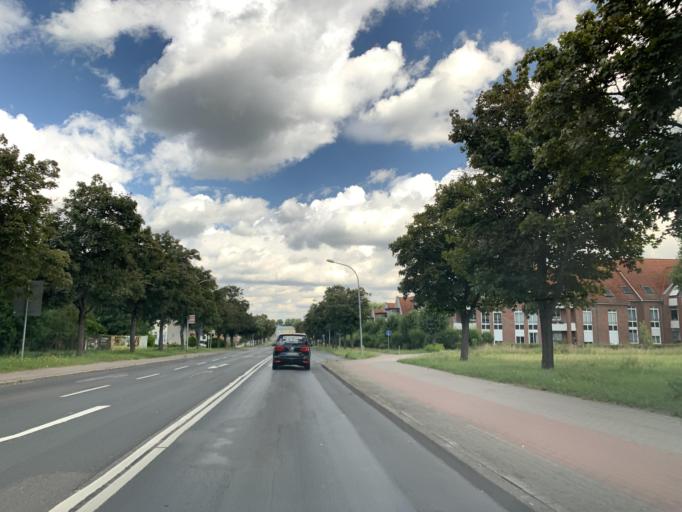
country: DE
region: Mecklenburg-Vorpommern
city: Neustrelitz
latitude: 53.3521
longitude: 13.0773
